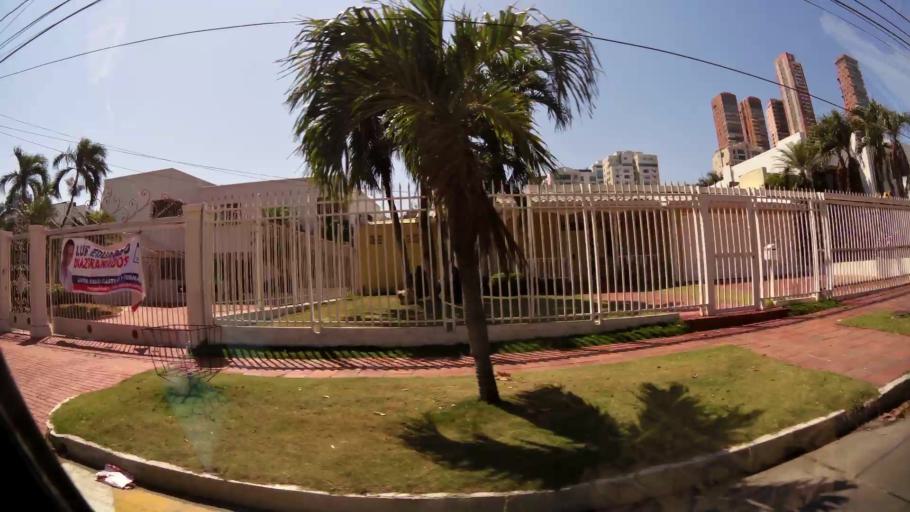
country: CO
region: Atlantico
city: Barranquilla
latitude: 11.0097
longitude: -74.8065
